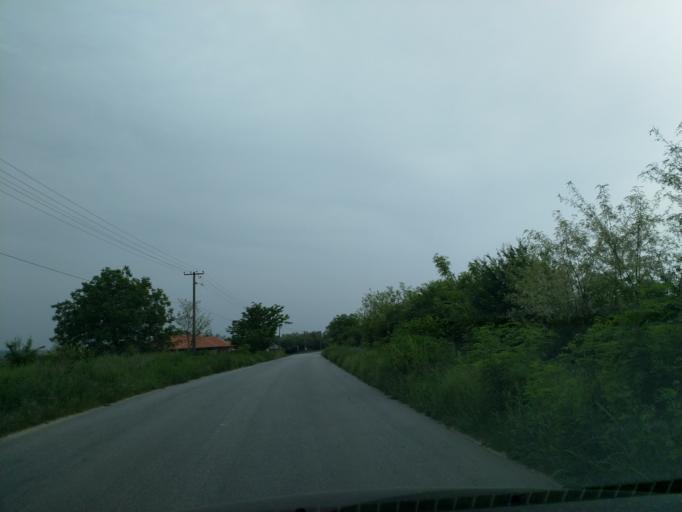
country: RS
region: Central Serbia
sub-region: Pomoravski Okrug
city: Jagodina
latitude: 43.9702
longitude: 21.2358
